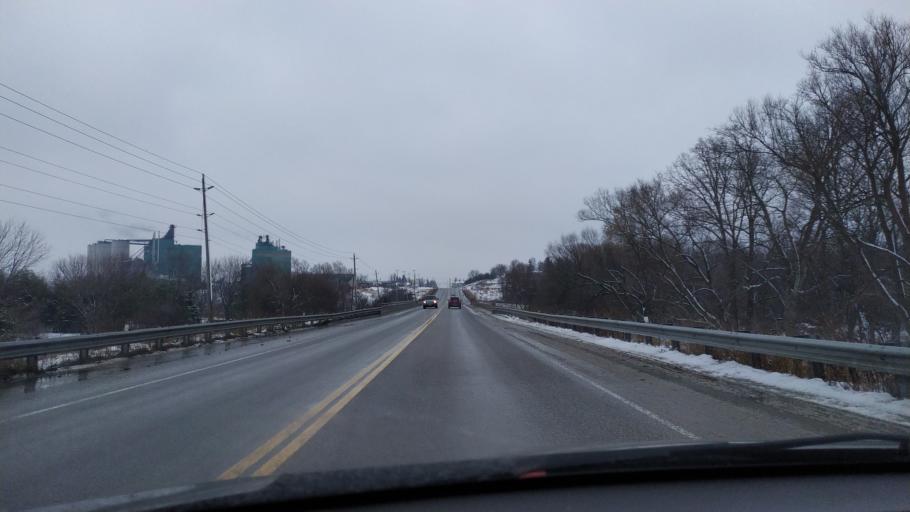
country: CA
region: Ontario
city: Waterloo
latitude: 43.6034
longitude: -80.6439
